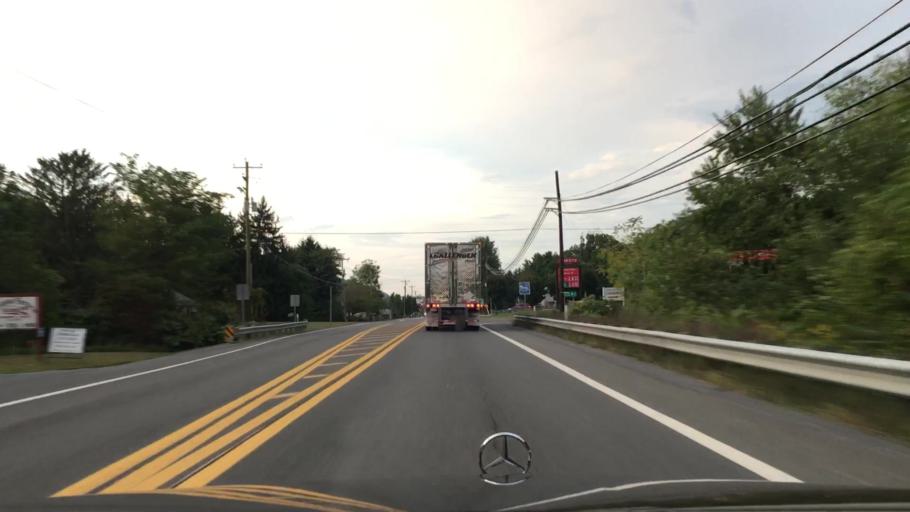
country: US
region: West Virginia
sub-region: Morgan County
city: Berkeley Springs
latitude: 39.5974
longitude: -78.2430
